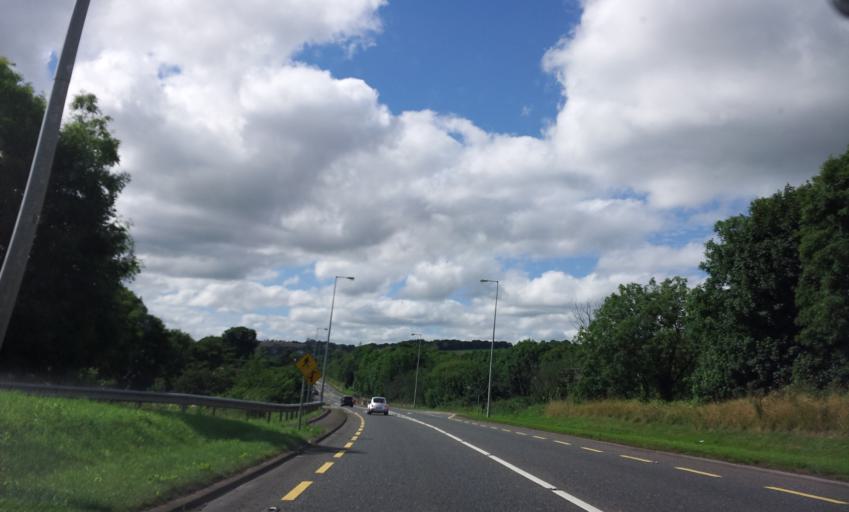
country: IE
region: Munster
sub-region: County Cork
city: Killumney
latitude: 51.8798
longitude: -8.6512
